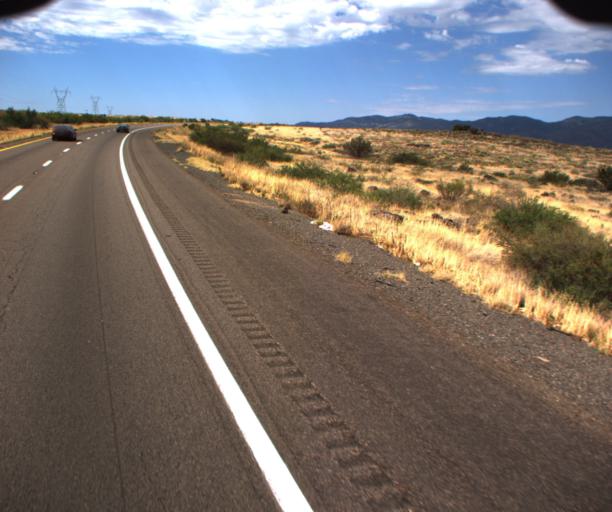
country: US
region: Arizona
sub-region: Yavapai County
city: Cordes Lakes
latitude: 34.2165
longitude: -112.1119
